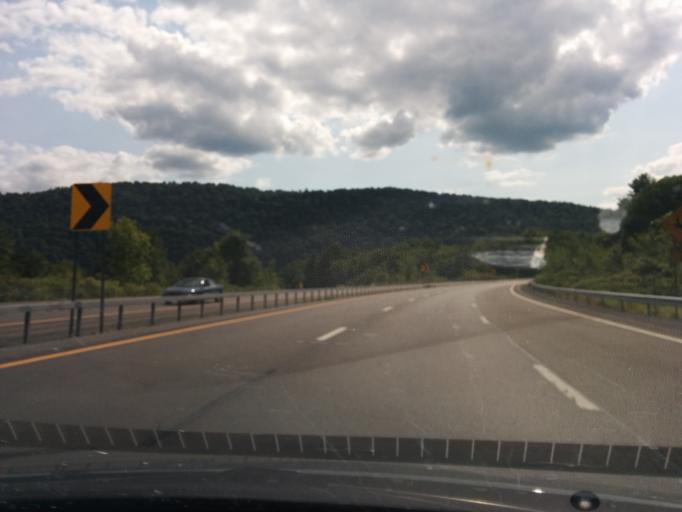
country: US
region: New York
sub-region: Delaware County
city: Hancock
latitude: 41.9707
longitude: -75.1780
